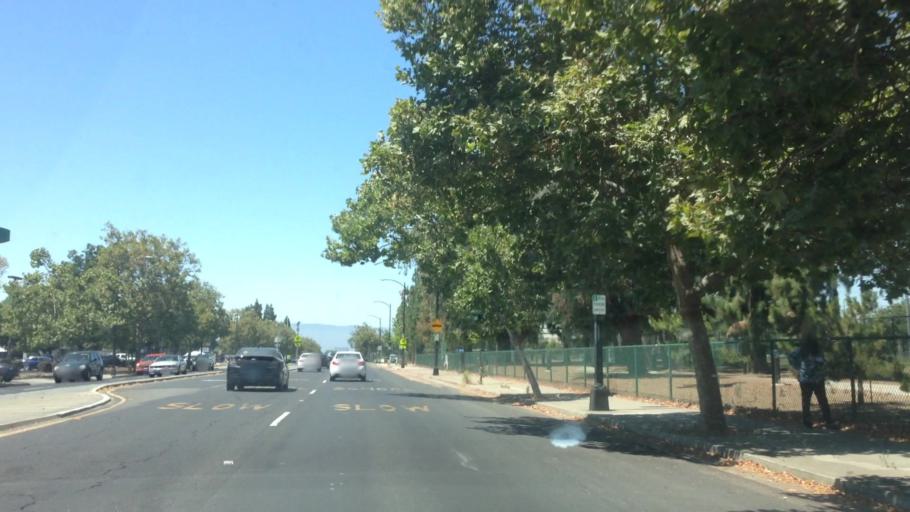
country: US
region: California
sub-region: Santa Clara County
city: Alum Rock
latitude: 37.3653
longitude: -121.8294
